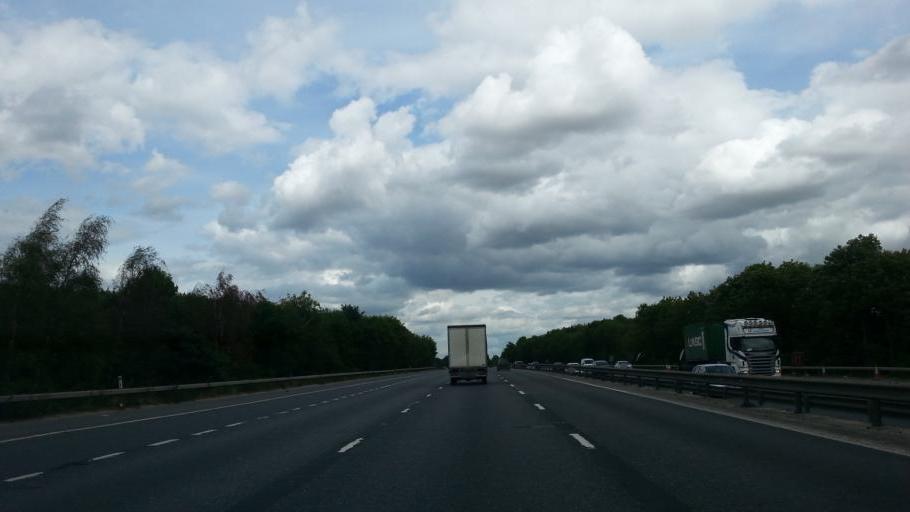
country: GB
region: England
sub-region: Essex
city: Harlow
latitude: 51.7469
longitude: 0.1406
